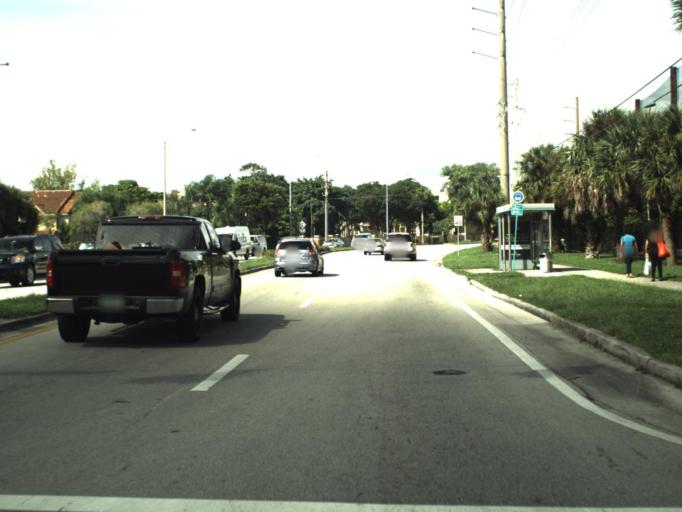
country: US
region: Florida
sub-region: Miami-Dade County
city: Country Club
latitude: 25.9421
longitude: -80.3136
